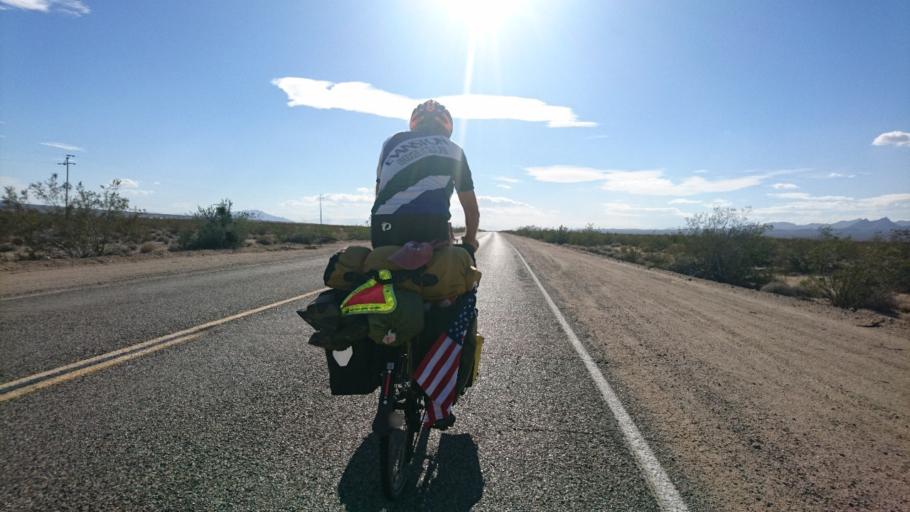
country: US
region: California
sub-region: San Bernardino County
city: Needles
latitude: 34.7266
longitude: -115.2611
